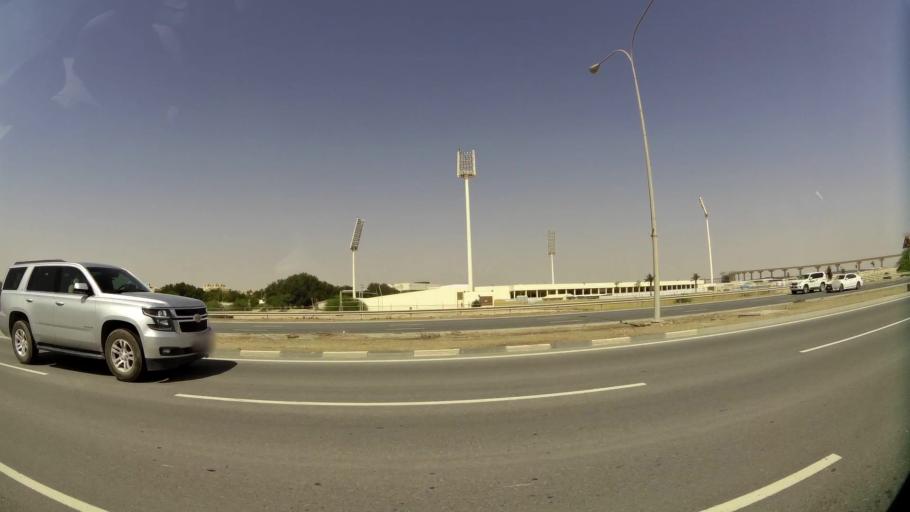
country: QA
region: Baladiyat ad Dawhah
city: Doha
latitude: 25.3742
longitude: 51.4978
